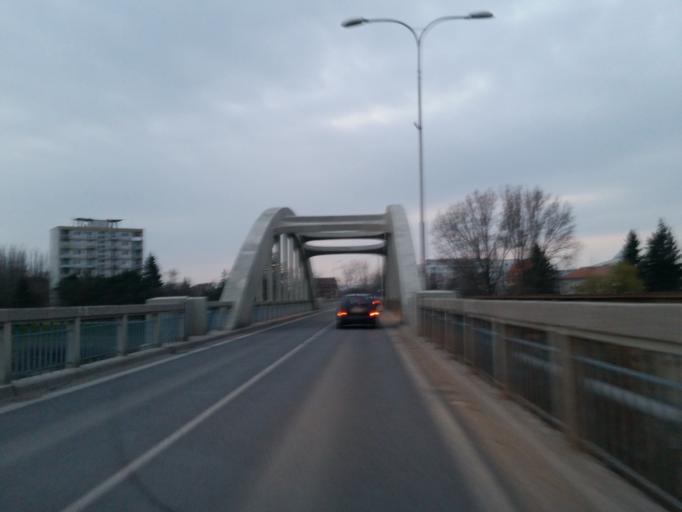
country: SK
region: Trnavsky
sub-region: Okres Trnava
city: Piestany
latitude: 48.5855
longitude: 17.8378
